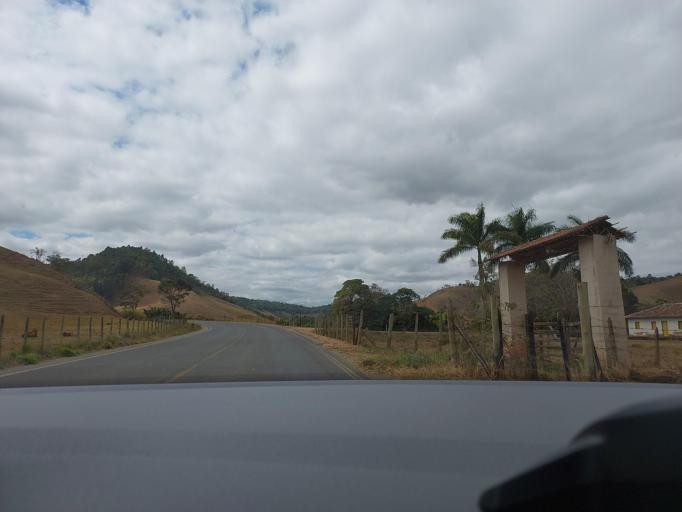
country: BR
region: Minas Gerais
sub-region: Vicosa
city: Vicosa
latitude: -20.8313
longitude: -42.7588
